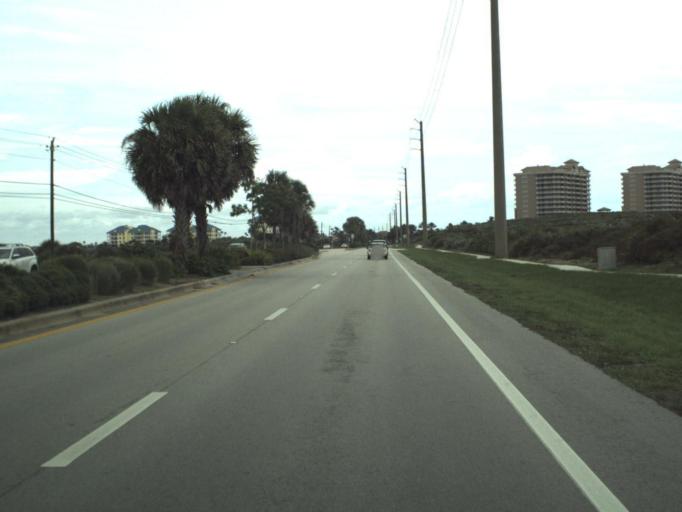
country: US
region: Florida
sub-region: Palm Beach County
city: Juno Beach
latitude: 26.8858
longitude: -80.0576
